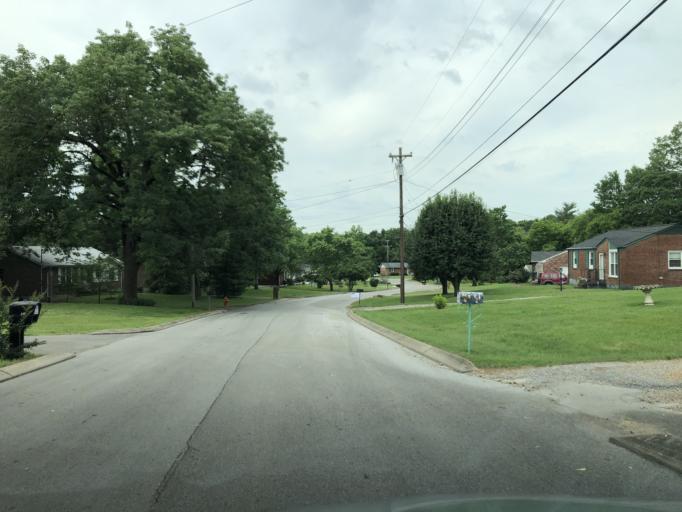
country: US
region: Tennessee
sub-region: Davidson County
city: Goodlettsville
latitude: 36.2870
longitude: -86.7116
